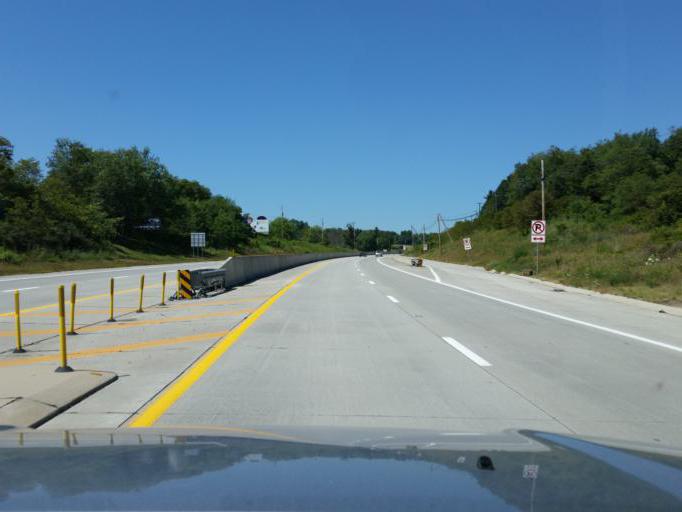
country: US
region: Pennsylvania
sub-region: Indiana County
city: Blairsville
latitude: 40.4301
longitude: -79.2922
